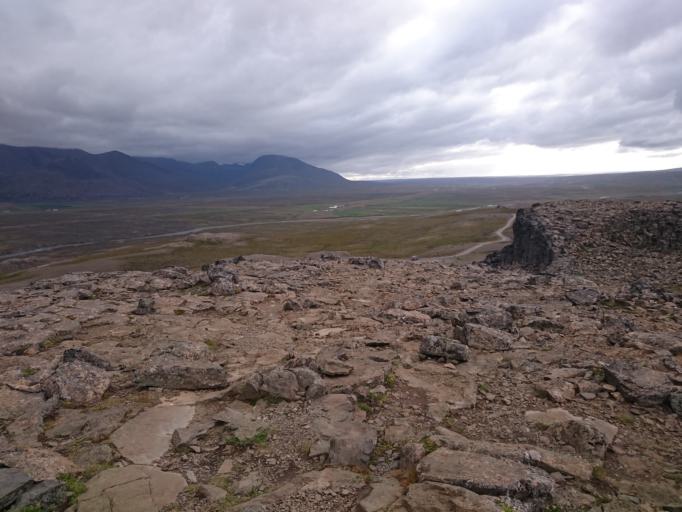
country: IS
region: Northwest
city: Saudarkrokur
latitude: 65.4752
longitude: -20.5966
